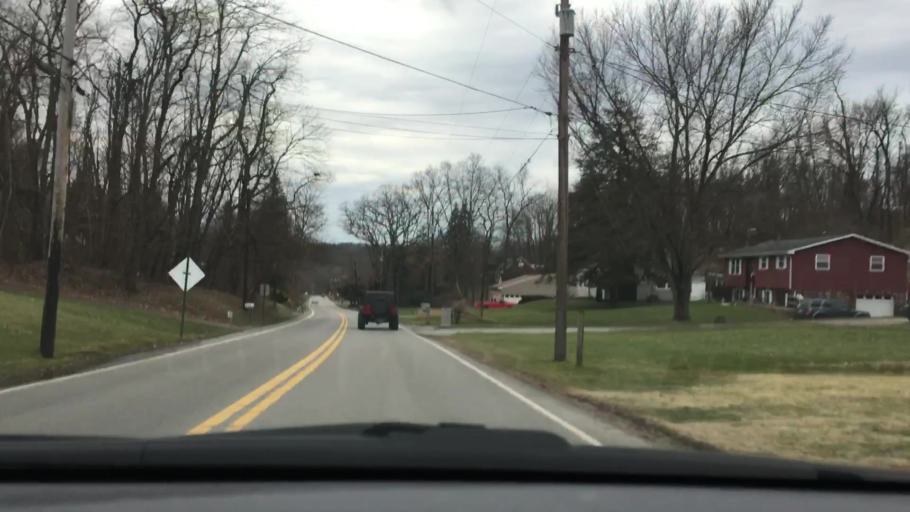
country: US
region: Pennsylvania
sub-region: Washington County
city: McDonald
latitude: 40.3548
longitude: -80.2414
